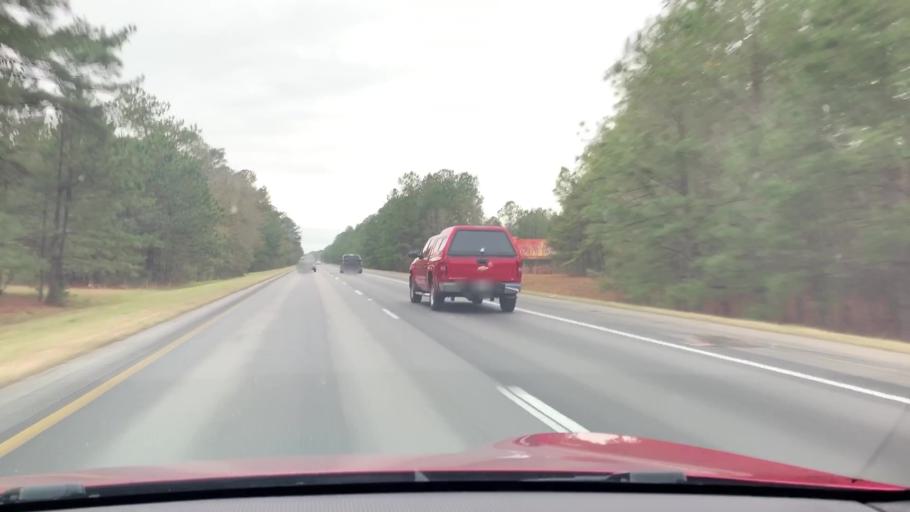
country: US
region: South Carolina
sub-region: Clarendon County
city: Manning
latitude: 33.6266
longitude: -80.2979
